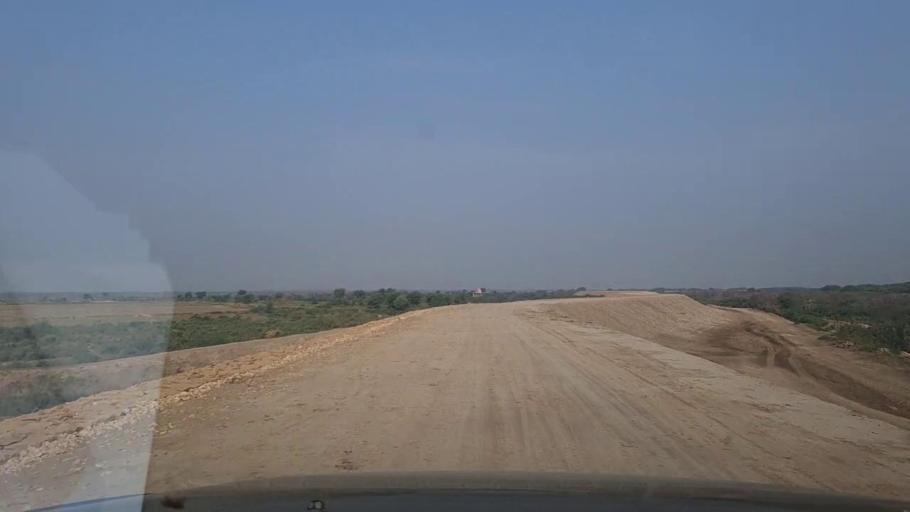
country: PK
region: Sindh
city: Bulri
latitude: 24.9613
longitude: 68.2920
